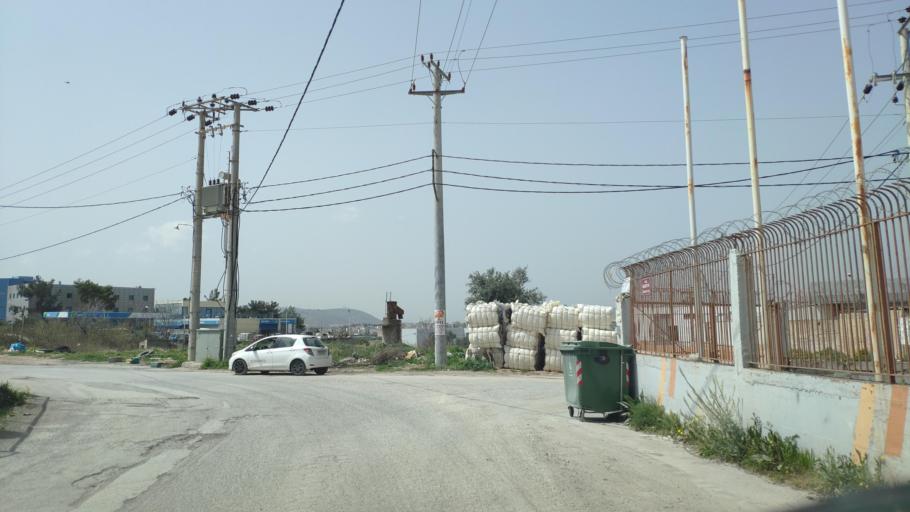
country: GR
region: Attica
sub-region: Nomarchia Athinas
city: Metamorfosi
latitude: 38.0742
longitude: 23.7650
